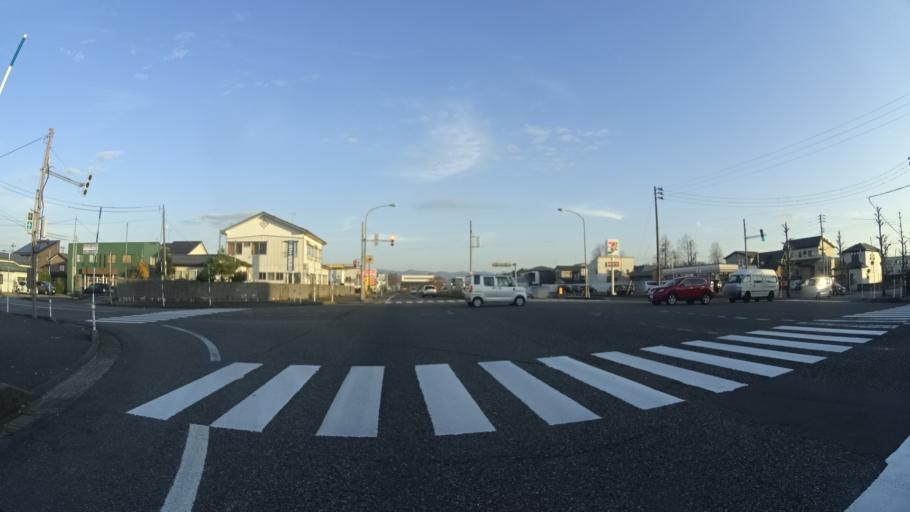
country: JP
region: Niigata
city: Nagaoka
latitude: 37.4465
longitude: 138.7751
